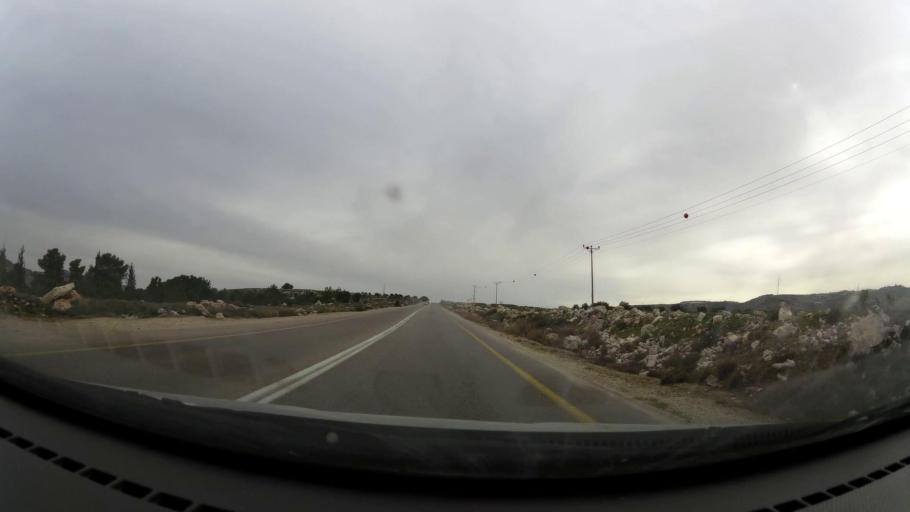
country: PS
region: West Bank
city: Surif
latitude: 31.6710
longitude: 35.0609
